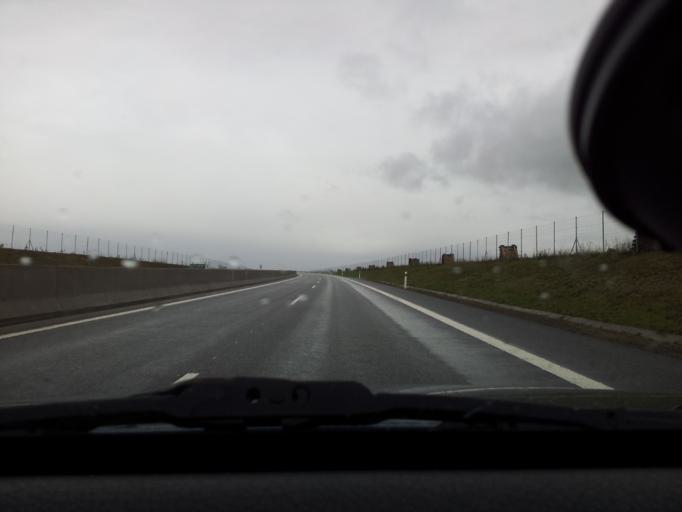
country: SK
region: Nitriansky
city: Zlate Moravce
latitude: 48.3529
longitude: 18.4656
